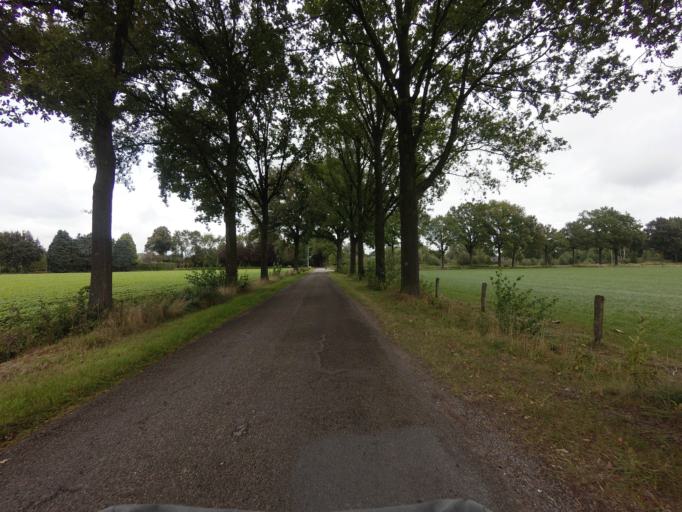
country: DE
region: North Rhine-Westphalia
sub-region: Regierungsbezirk Munster
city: Gronau
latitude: 52.2304
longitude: 7.0319
